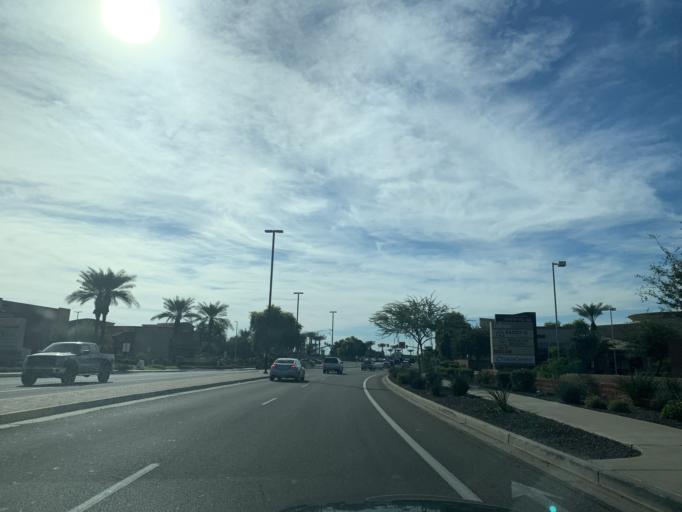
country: US
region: Arizona
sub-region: Maricopa County
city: Gilbert
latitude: 33.3004
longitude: -111.7440
